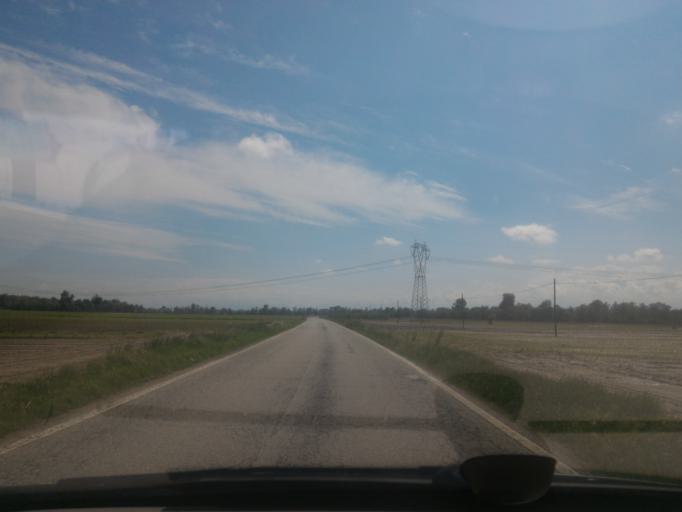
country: IT
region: Piedmont
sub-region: Provincia di Torino
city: Pancalieri
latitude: 44.8238
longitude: 7.5873
